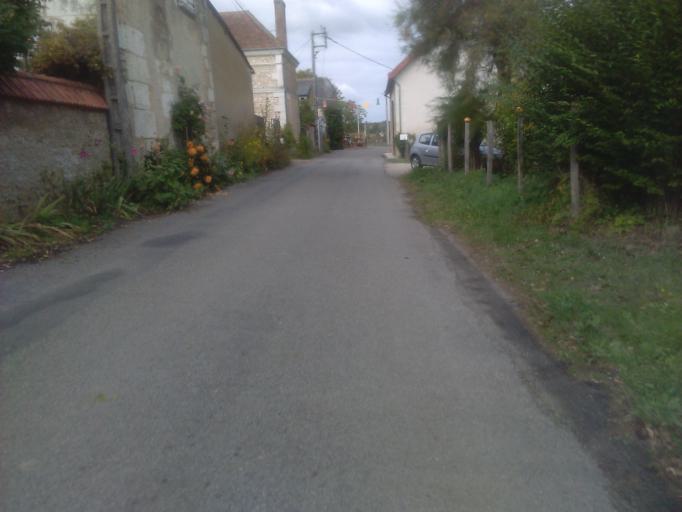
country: FR
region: Centre
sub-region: Departement du Loir-et-Cher
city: Villiers-sur-Loir
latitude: 47.8026
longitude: 0.9785
